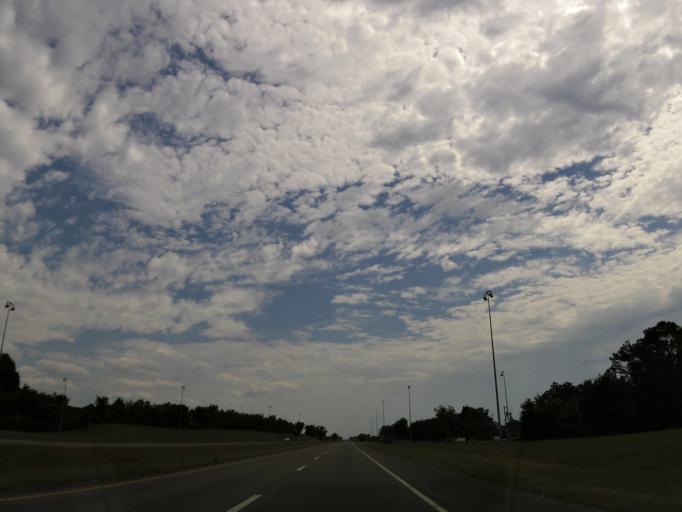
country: US
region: Alabama
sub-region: Jackson County
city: Stevenson
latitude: 34.8531
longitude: -85.8239
